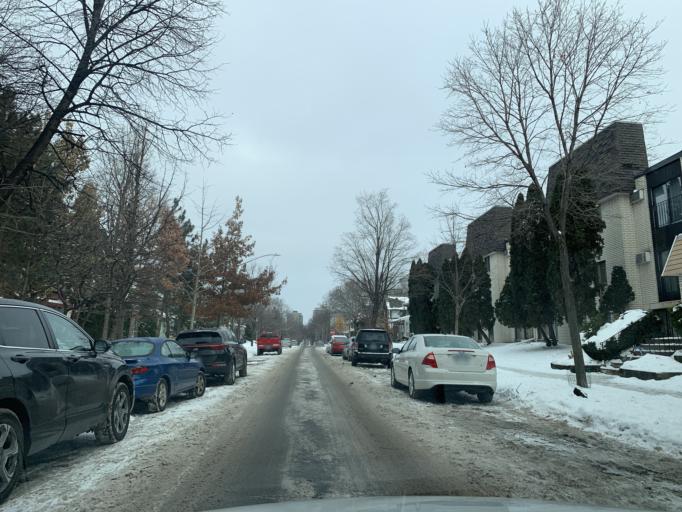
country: US
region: Minnesota
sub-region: Hennepin County
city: Minneapolis
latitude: 44.9563
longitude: -93.2855
